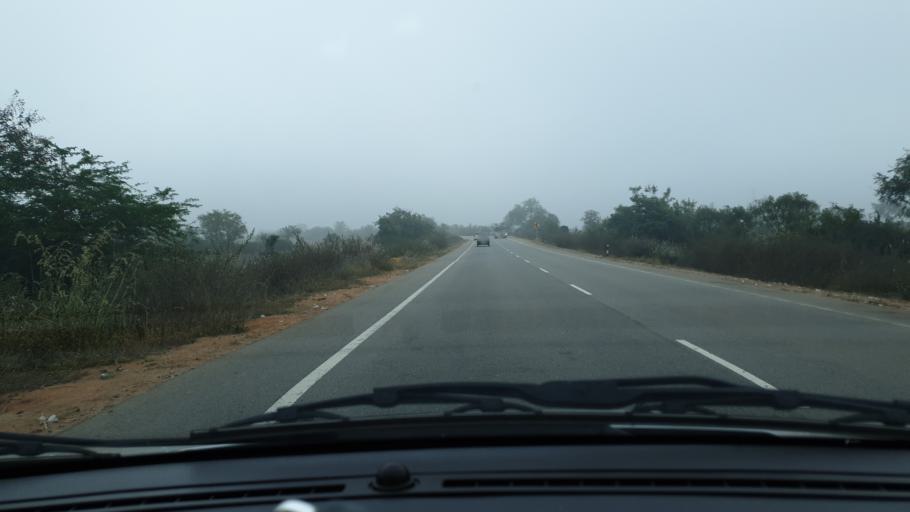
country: IN
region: Telangana
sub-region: Nalgonda
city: Devarkonda
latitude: 16.6315
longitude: 78.6428
